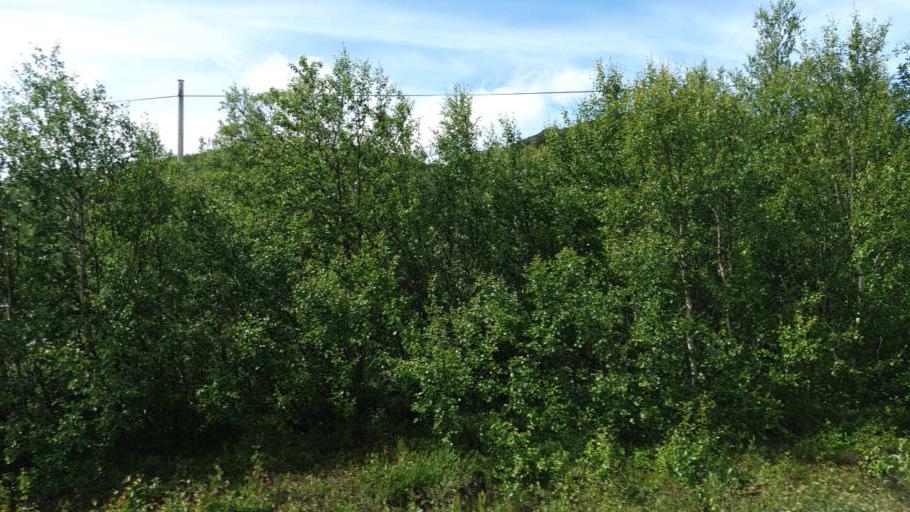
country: NO
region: Oppland
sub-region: Oystre Slidre
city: Heggenes
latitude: 61.5002
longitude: 8.8426
